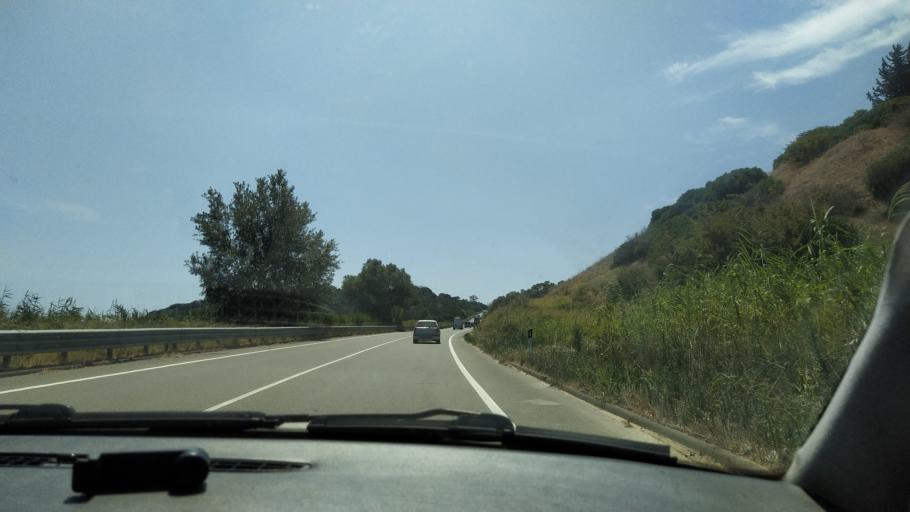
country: IT
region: Apulia
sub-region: Provincia di Taranto
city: Marina di Ginosa
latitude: 40.4314
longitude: 16.7929
